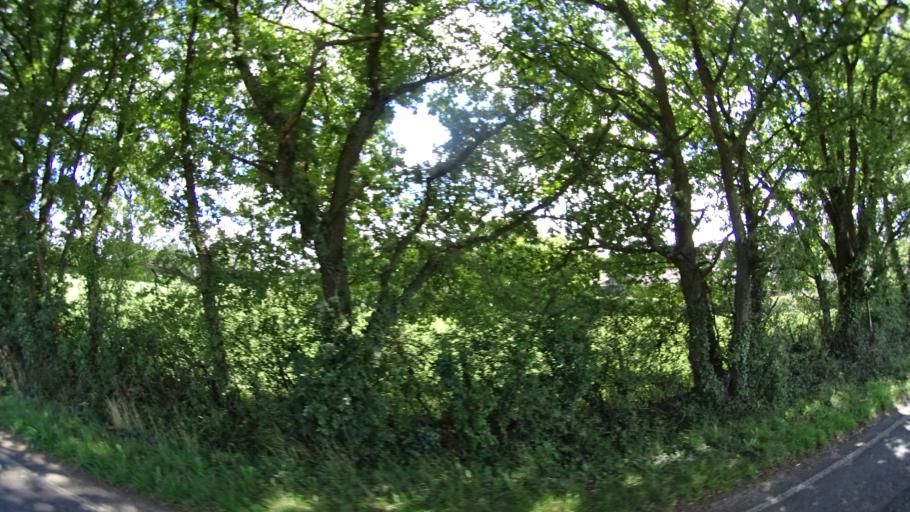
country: GB
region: England
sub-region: Hampshire
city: Romsey
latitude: 51.0184
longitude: -1.4678
